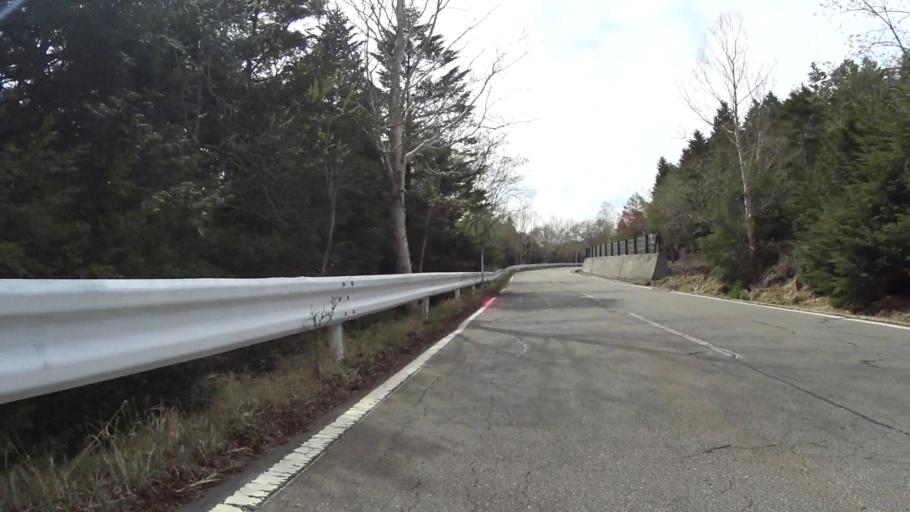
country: JP
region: Nagano
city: Chino
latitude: 36.0568
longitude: 138.3304
